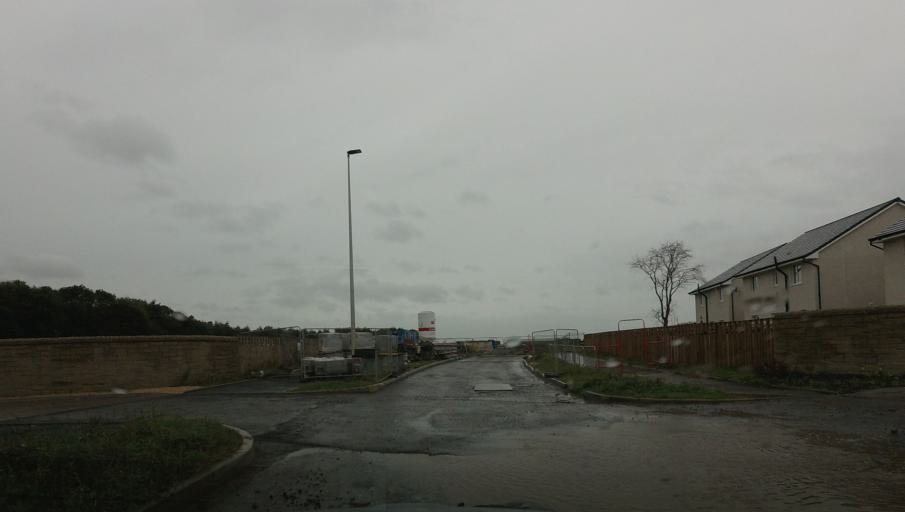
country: GB
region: Scotland
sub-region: West Lothian
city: East Calder
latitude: 55.9026
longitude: -3.4567
